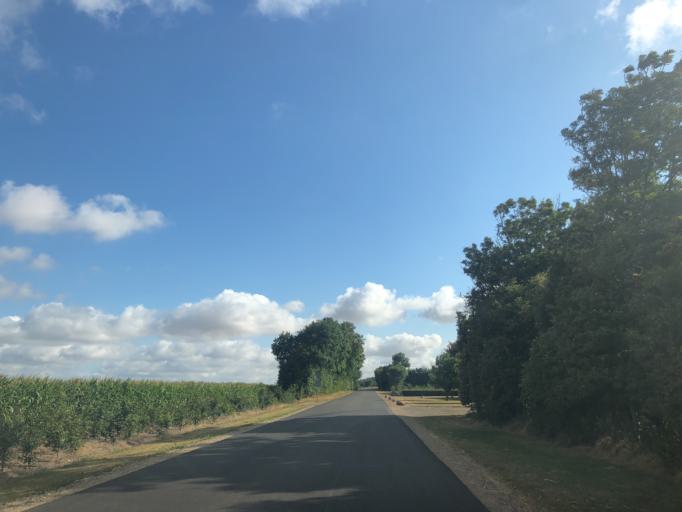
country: DK
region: Central Jutland
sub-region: Holstebro Kommune
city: Vinderup
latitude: 56.6164
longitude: 8.8693
